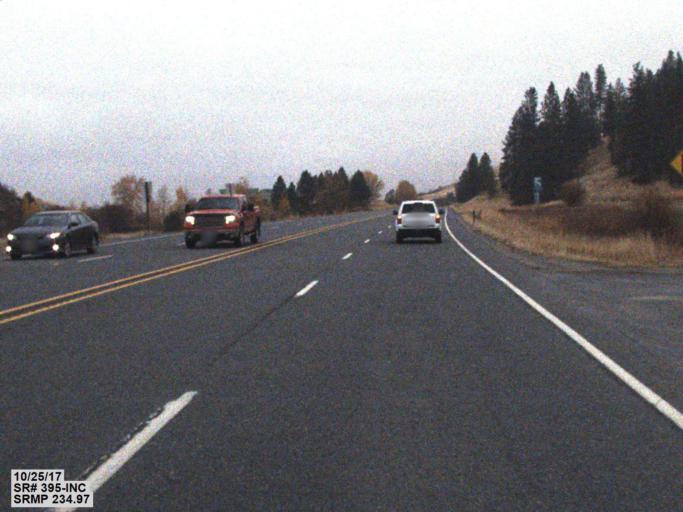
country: US
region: Washington
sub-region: Stevens County
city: Kettle Falls
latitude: 48.5913
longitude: -117.9952
